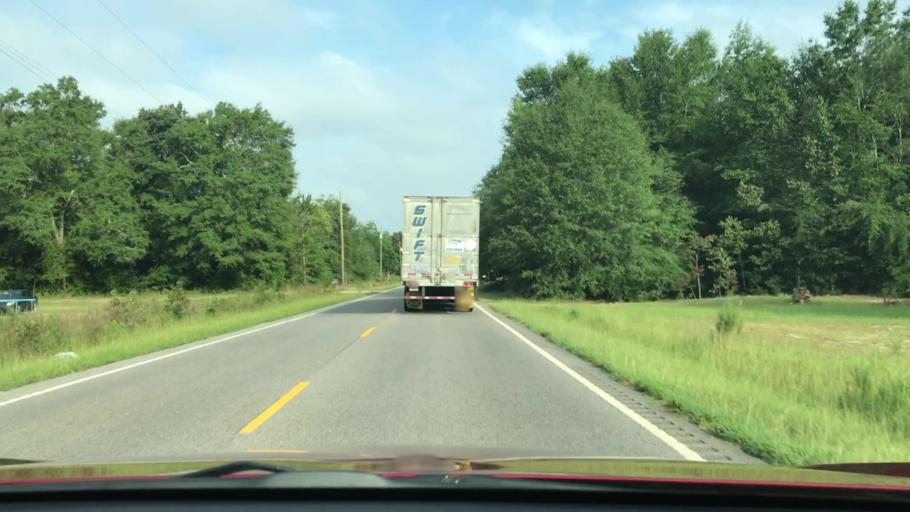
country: US
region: South Carolina
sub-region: Barnwell County
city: Williston
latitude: 33.6317
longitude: -81.3089
